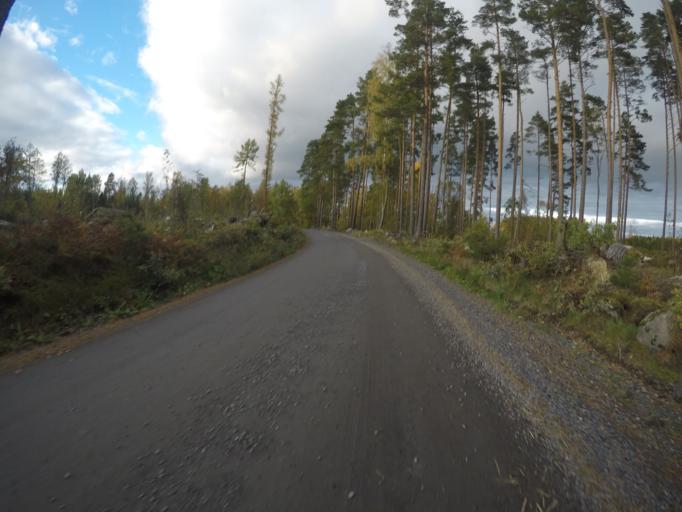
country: SE
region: Vaestmanland
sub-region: Arboga Kommun
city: Tyringe
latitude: 59.2934
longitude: 15.9850
